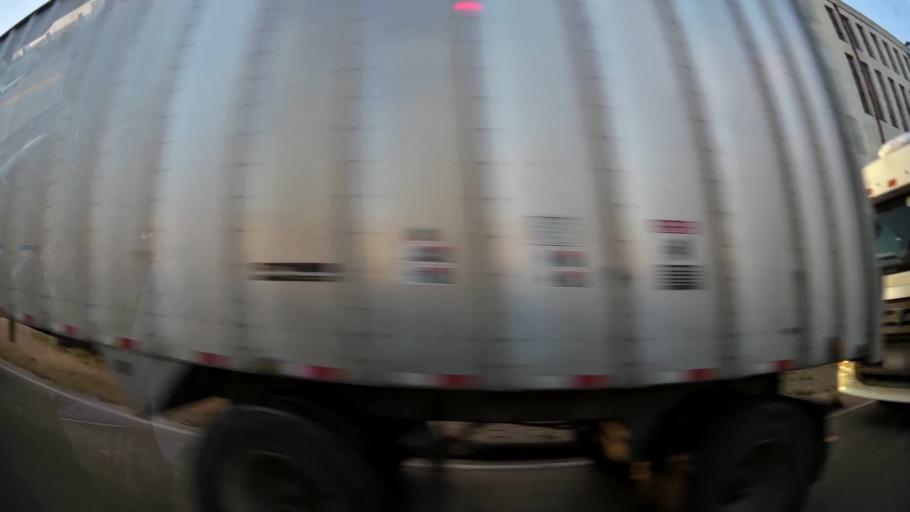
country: UY
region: Montevideo
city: Montevideo
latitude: -34.8872
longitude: -56.1981
